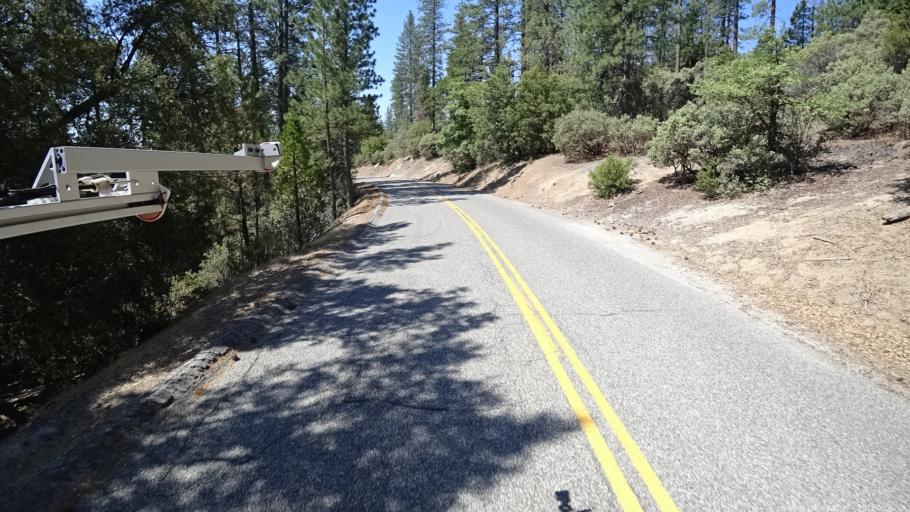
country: US
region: California
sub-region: Madera County
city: Oakhurst
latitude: 37.3868
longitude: -119.3577
